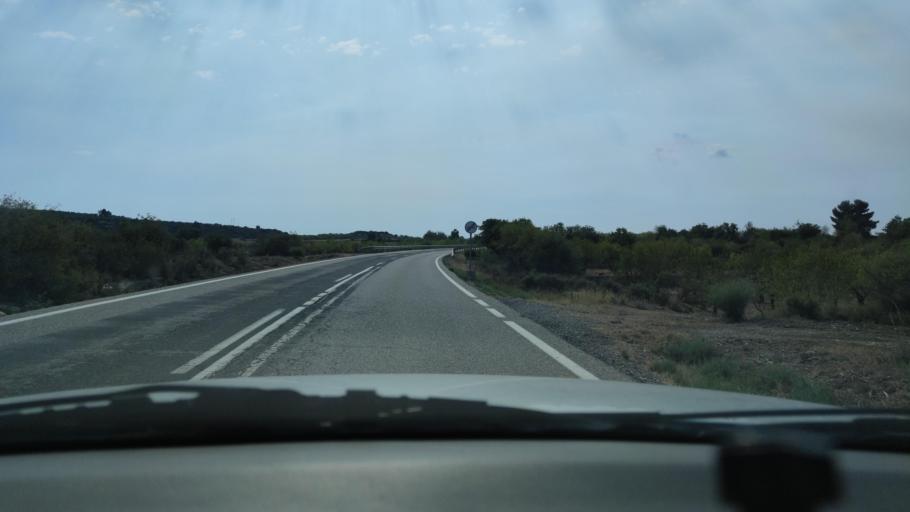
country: ES
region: Catalonia
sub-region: Provincia de Lleida
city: Arbeca
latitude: 41.5054
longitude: 0.9306
